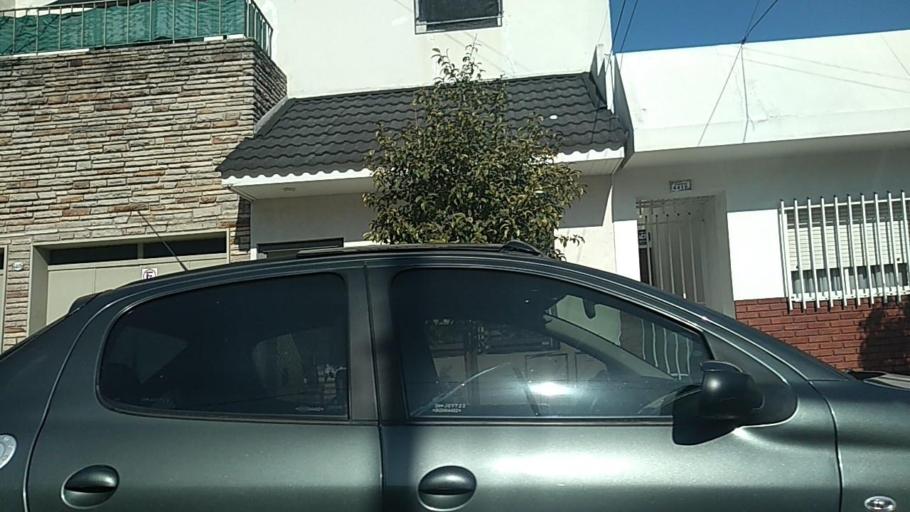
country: AR
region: Buenos Aires F.D.
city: Villa Santa Rita
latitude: -34.6084
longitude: -58.5113
